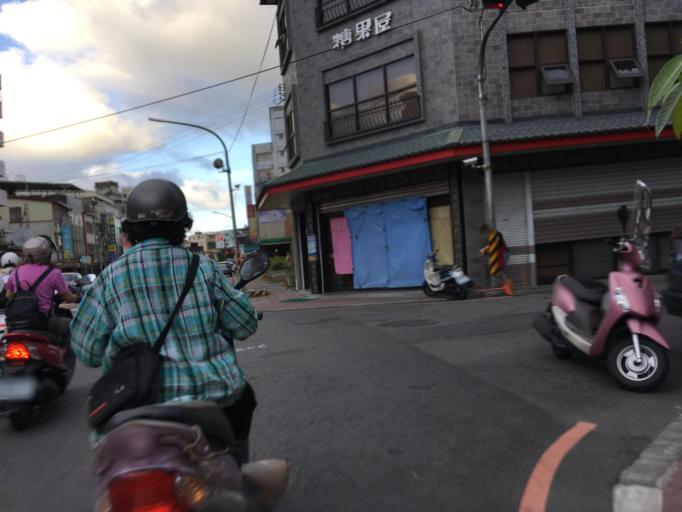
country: TW
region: Taiwan
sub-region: Yilan
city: Yilan
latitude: 24.6729
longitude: 121.7680
